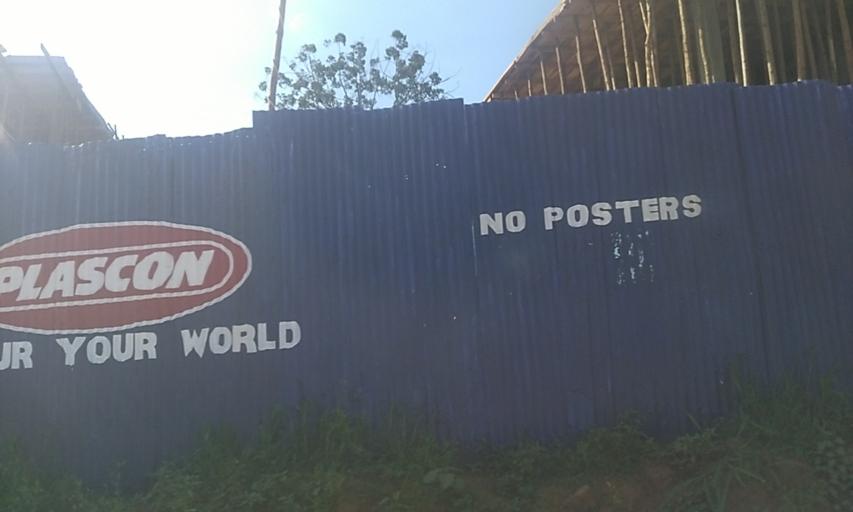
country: UG
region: Central Region
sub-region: Wakiso District
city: Kireka
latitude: 0.3585
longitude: 32.6165
